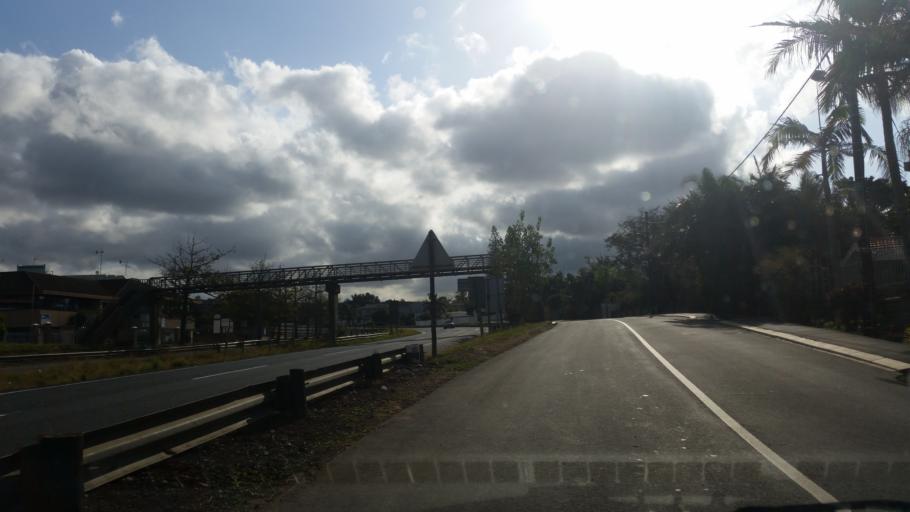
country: ZA
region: KwaZulu-Natal
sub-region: eThekwini Metropolitan Municipality
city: Berea
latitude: -29.8303
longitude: 30.9527
